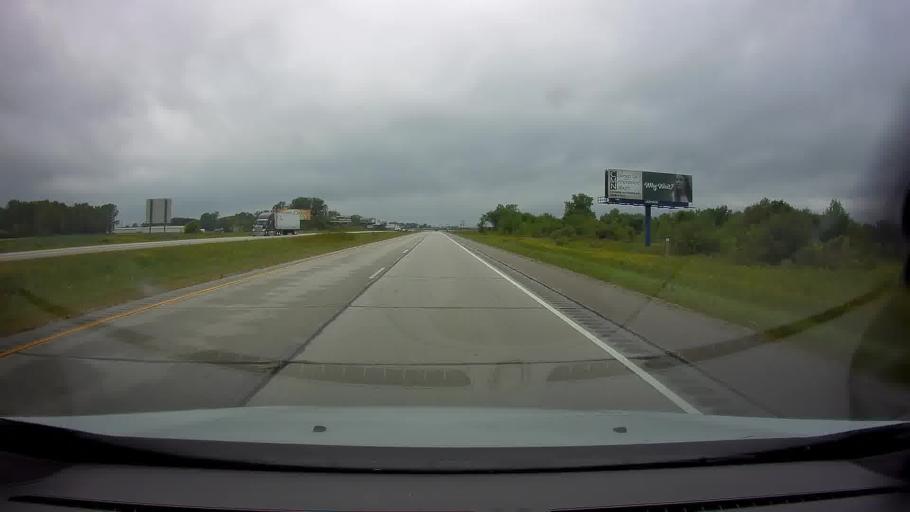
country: US
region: Wisconsin
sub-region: Brown County
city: Pulaski
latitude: 44.5990
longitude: -88.2329
